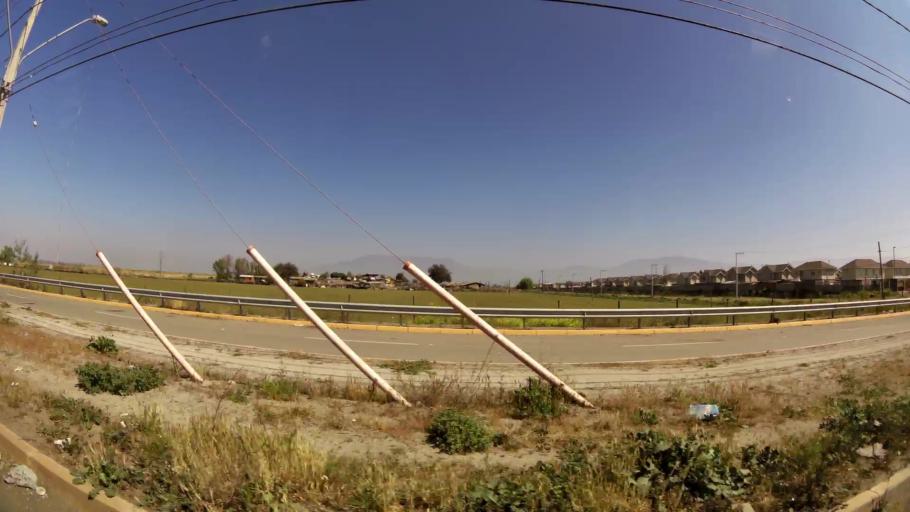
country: CL
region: Santiago Metropolitan
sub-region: Provincia de Chacabuco
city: Chicureo Abajo
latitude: -33.3309
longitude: -70.7453
